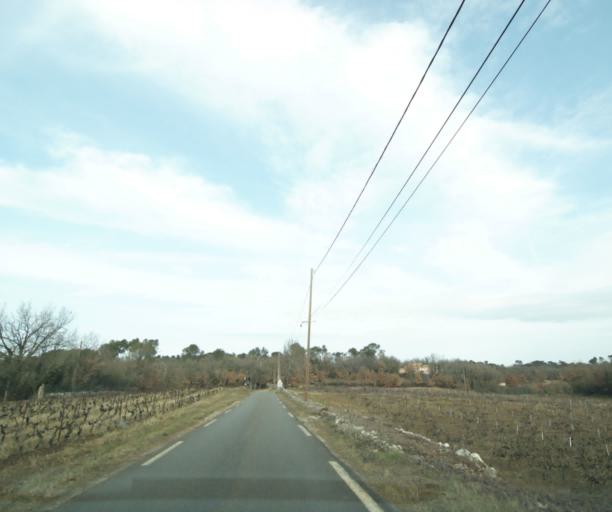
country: FR
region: Provence-Alpes-Cote d'Azur
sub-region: Departement du Var
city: Rougiers
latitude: 43.4082
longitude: 5.8769
